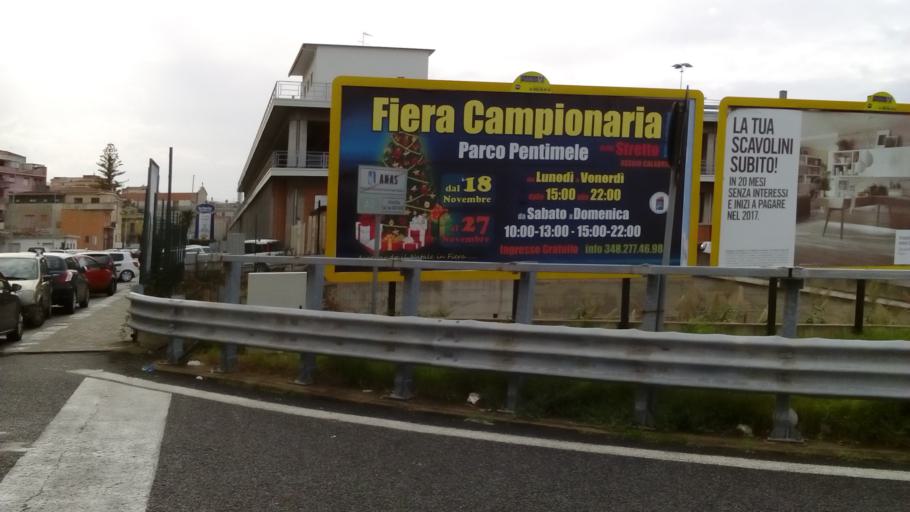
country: IT
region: Calabria
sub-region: Provincia di Reggio Calabria
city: Campo Calabro
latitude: 38.2143
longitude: 15.6369
